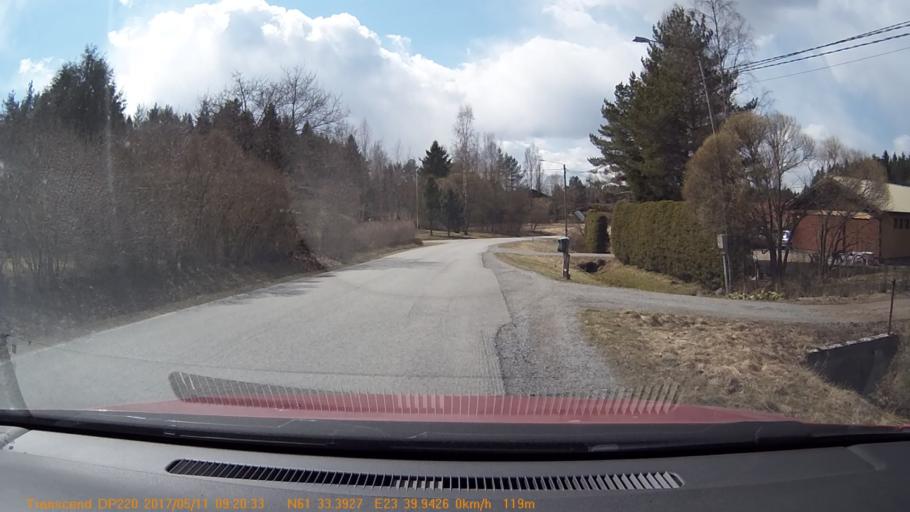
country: FI
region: Pirkanmaa
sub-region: Tampere
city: Yloejaervi
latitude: 61.5566
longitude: 23.6657
